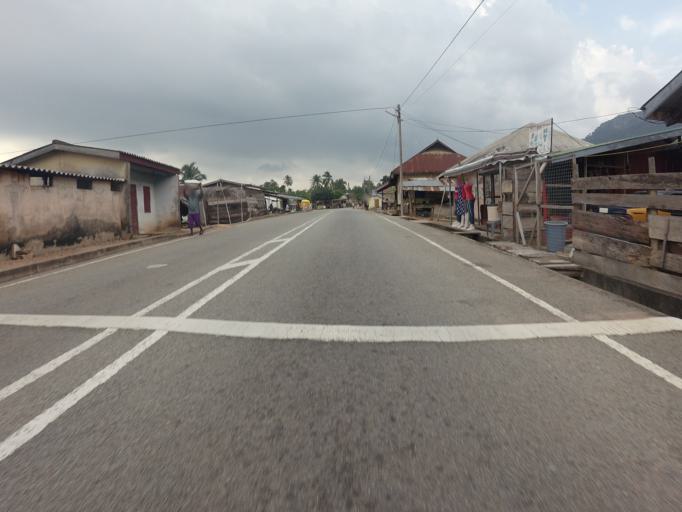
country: GH
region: Volta
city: Ho
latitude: 6.7697
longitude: 0.4810
